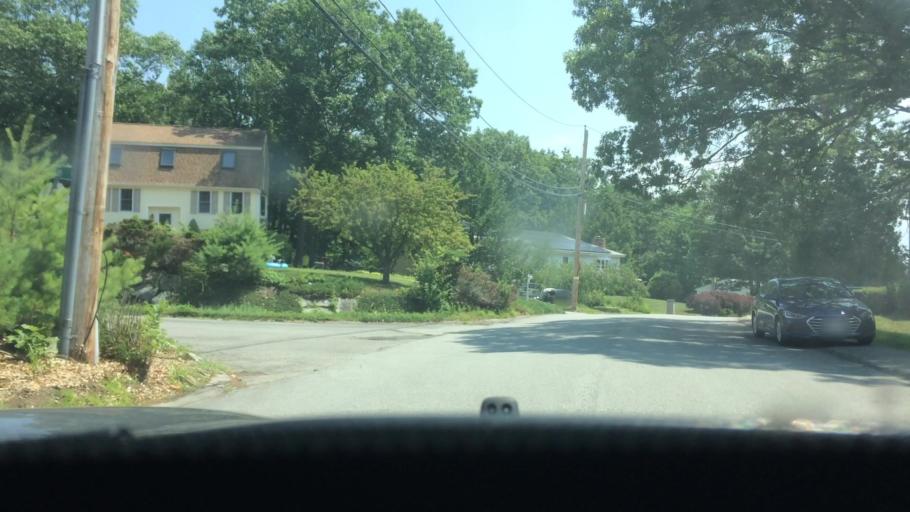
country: US
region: Massachusetts
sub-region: Middlesex County
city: Lowell
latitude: 42.6520
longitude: -71.3528
